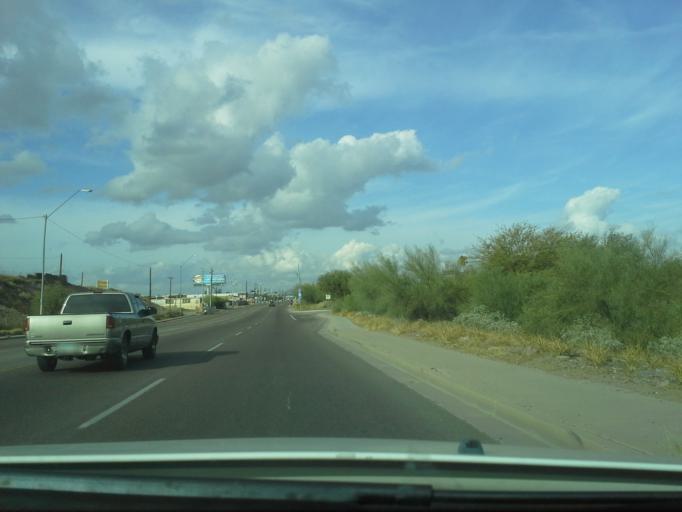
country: US
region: Arizona
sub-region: Maricopa County
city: Phoenix
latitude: 33.4202
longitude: -112.0823
